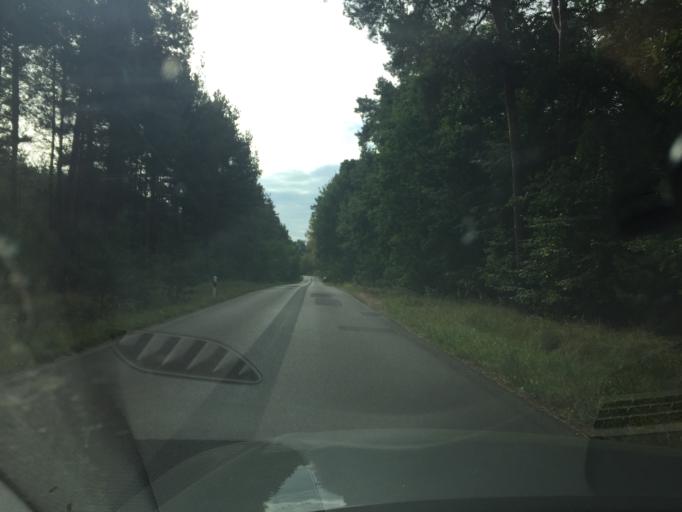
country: DE
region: Brandenburg
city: Erkner
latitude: 52.3953
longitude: 13.7645
